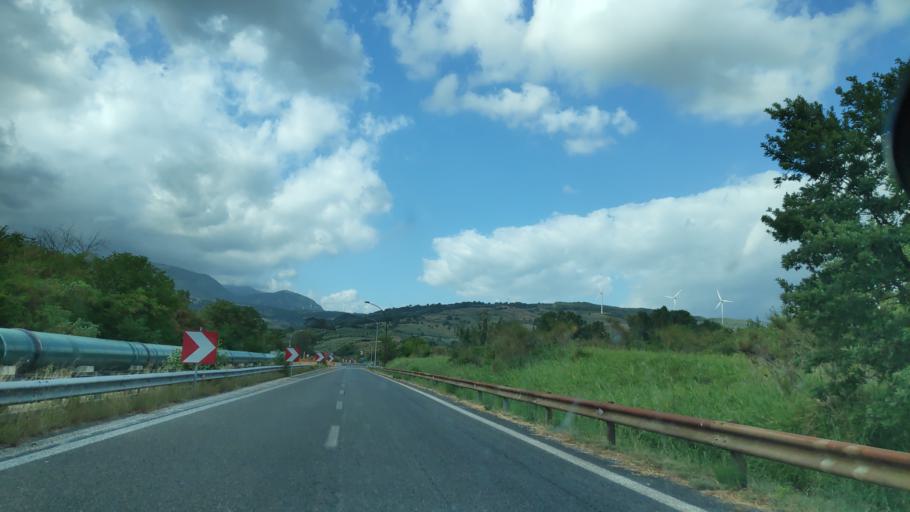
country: IT
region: Campania
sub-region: Provincia di Salerno
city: Serre
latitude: 40.6204
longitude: 15.1815
